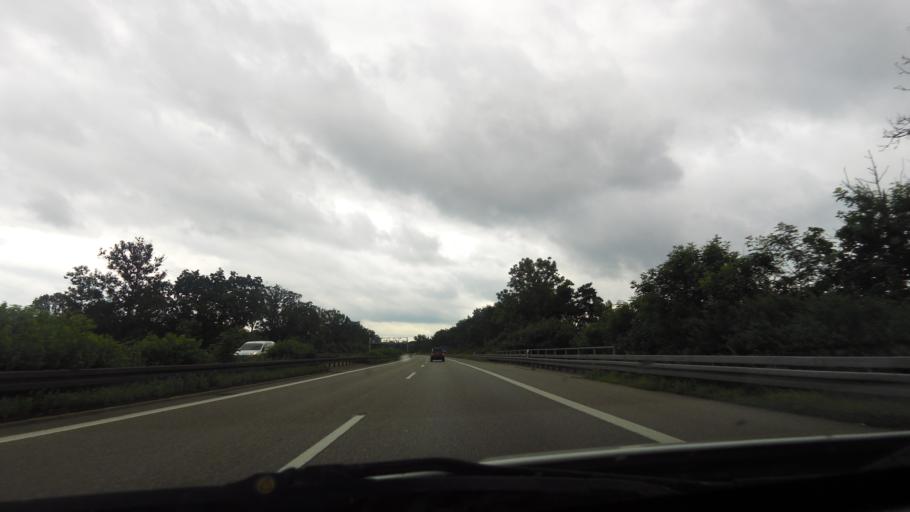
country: DE
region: Bavaria
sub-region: Swabia
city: Heimertingen
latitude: 48.0221
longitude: 10.1325
